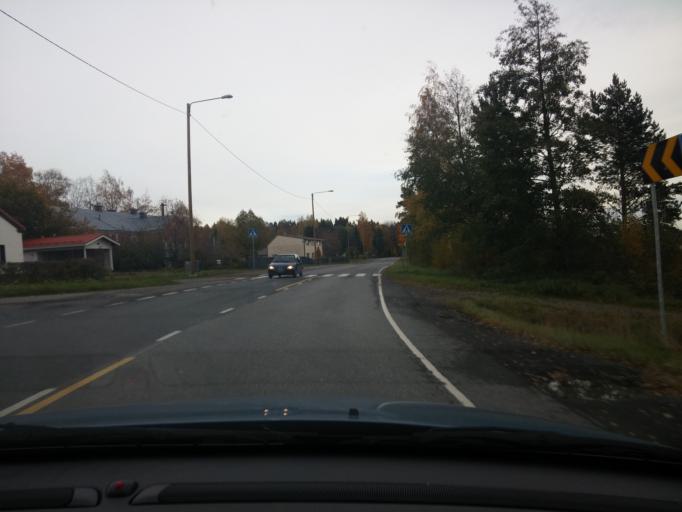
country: FI
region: Haeme
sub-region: Forssa
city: Tammela
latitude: 60.8062
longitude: 23.7949
